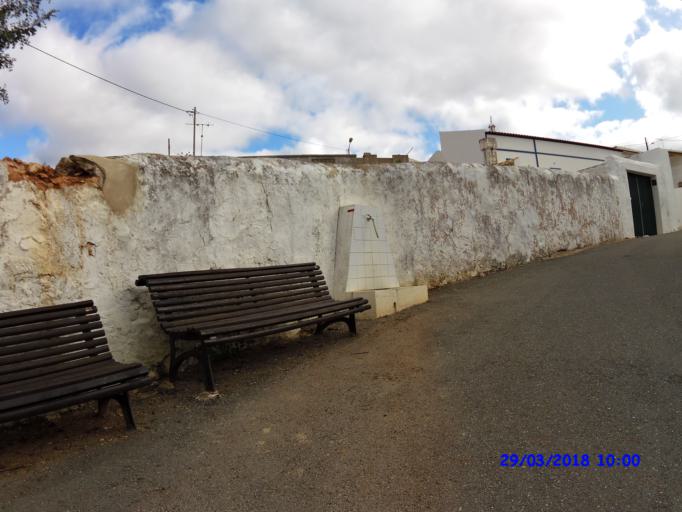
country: PT
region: Faro
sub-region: Loule
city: Boliqueime
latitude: 37.2304
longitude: -8.1638
